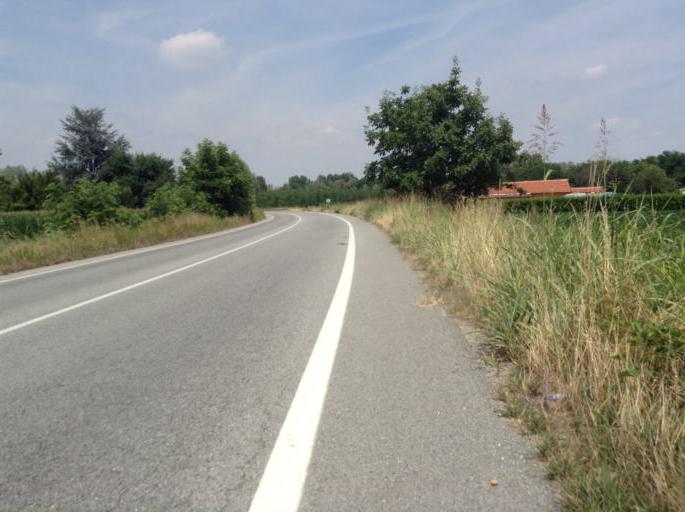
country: IT
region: Piedmont
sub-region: Provincia di Torino
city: Carignano
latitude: 44.9115
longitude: 7.6806
